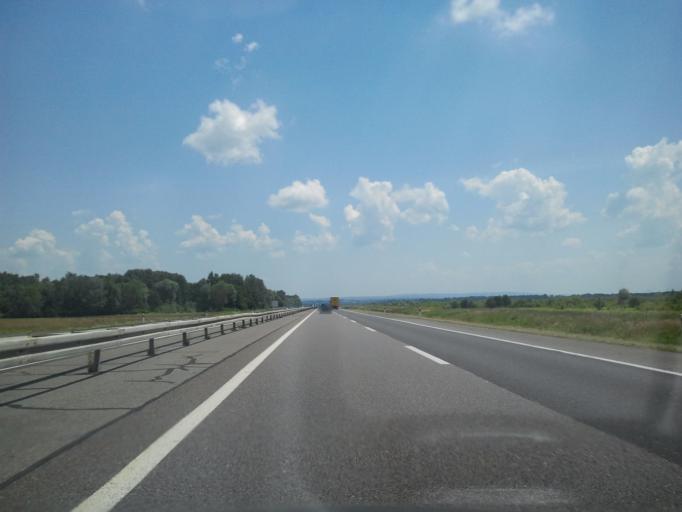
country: HR
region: Zagrebacka
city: Kriz
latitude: 45.6846
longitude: 16.4163
